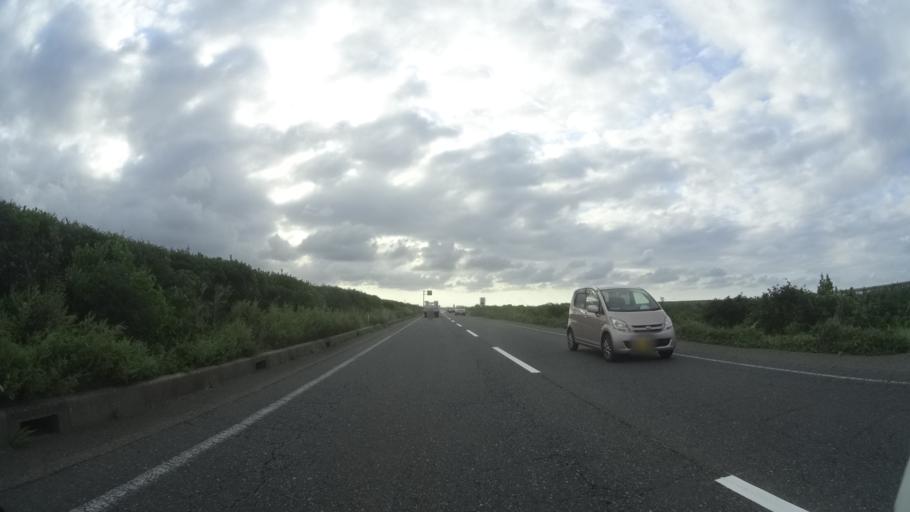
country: JP
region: Tottori
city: Kurayoshi
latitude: 35.5005
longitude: 133.7415
